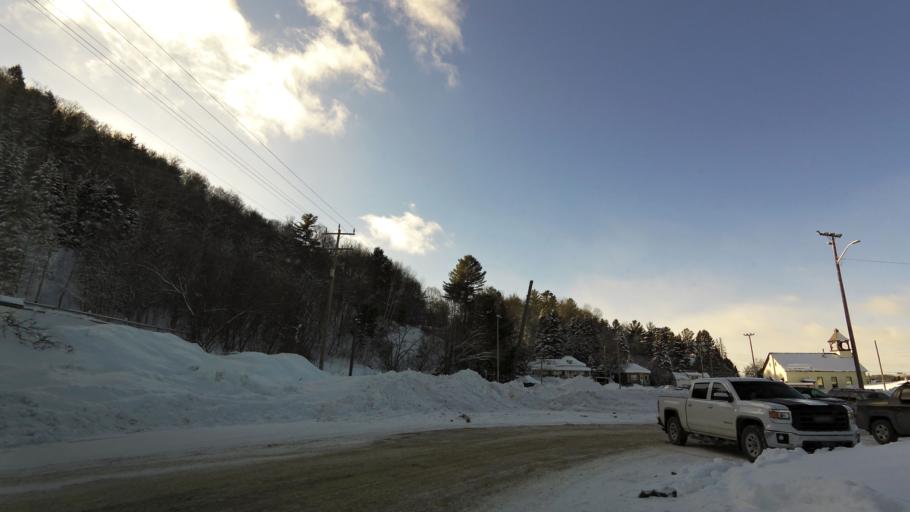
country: CA
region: Ontario
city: Bancroft
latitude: 45.0450
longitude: -78.5061
